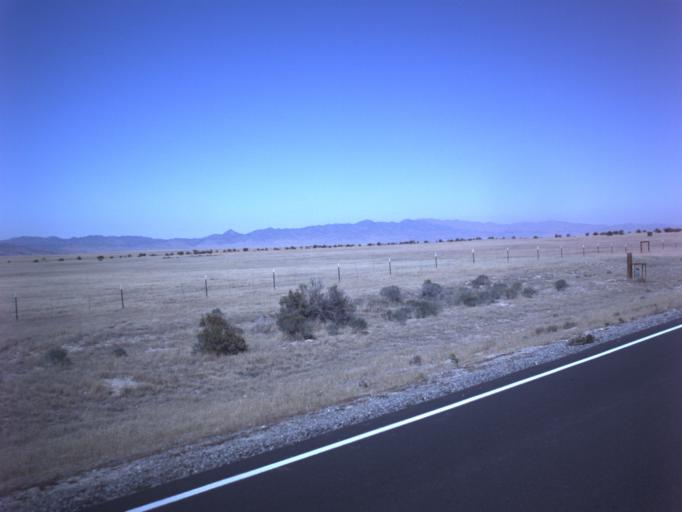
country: US
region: Utah
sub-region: Tooele County
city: Grantsville
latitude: 40.2831
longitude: -112.7419
